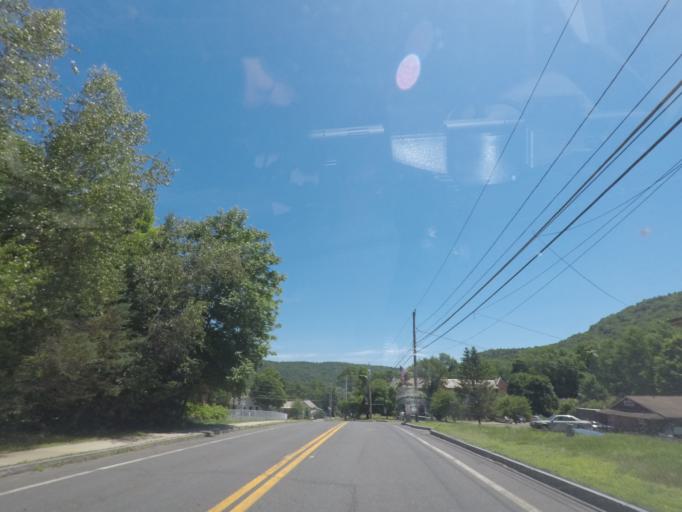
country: US
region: Massachusetts
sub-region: Berkshire County
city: Becket
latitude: 42.2797
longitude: -72.9841
